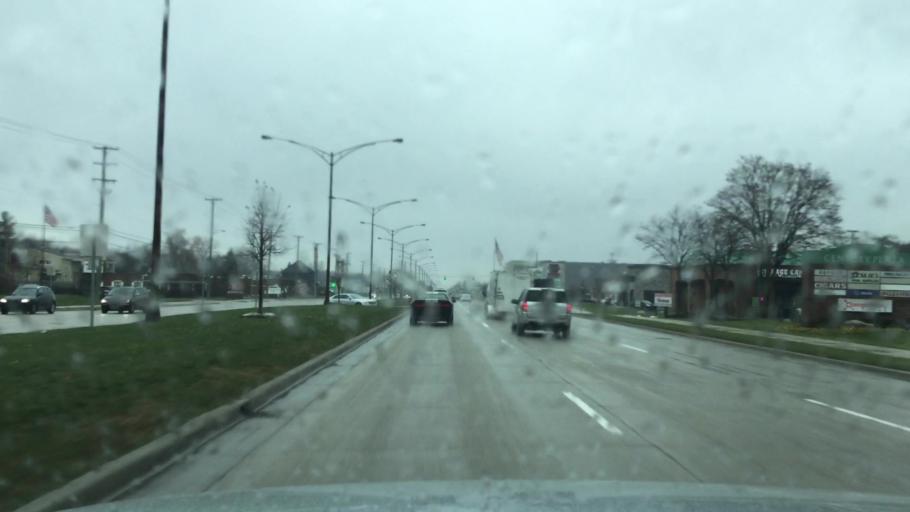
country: US
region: Michigan
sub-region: Oakland County
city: Troy
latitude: 42.5712
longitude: -83.1280
